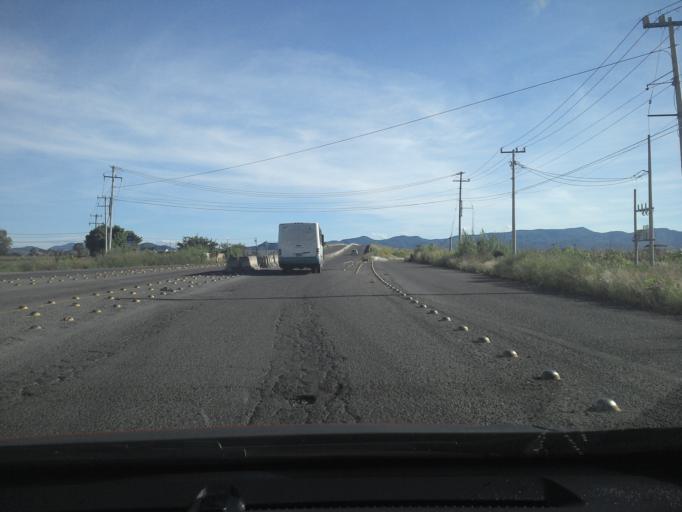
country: MX
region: Jalisco
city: El Refugio
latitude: 20.6603
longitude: -103.7341
